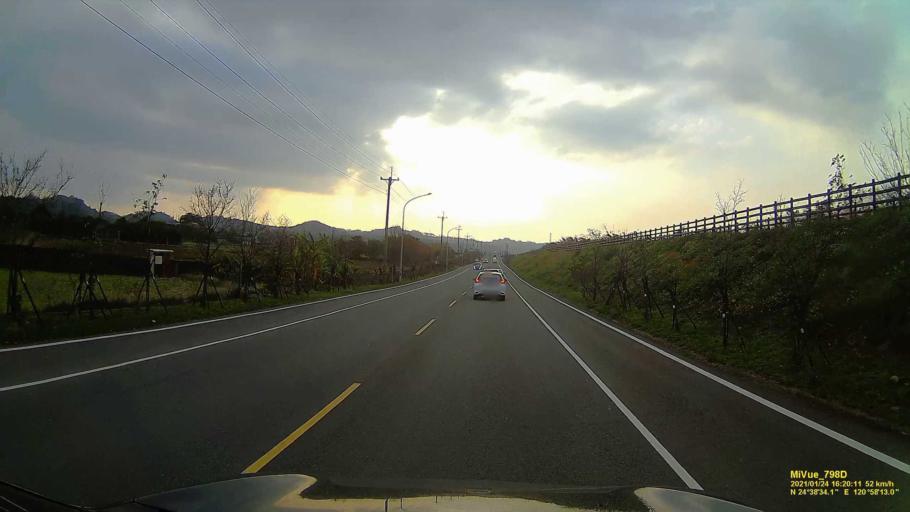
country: TW
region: Taiwan
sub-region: Hsinchu
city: Hsinchu
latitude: 24.6426
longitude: 120.9694
